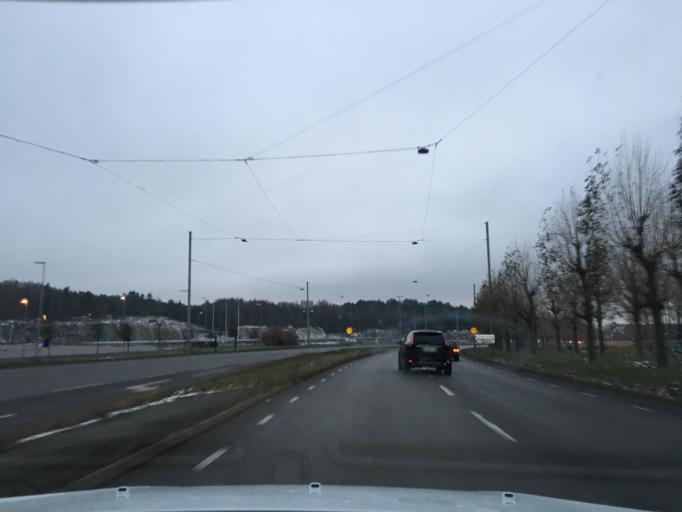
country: SE
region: Vaestra Goetaland
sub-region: Goteborg
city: Majorna
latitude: 57.7171
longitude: 11.8478
